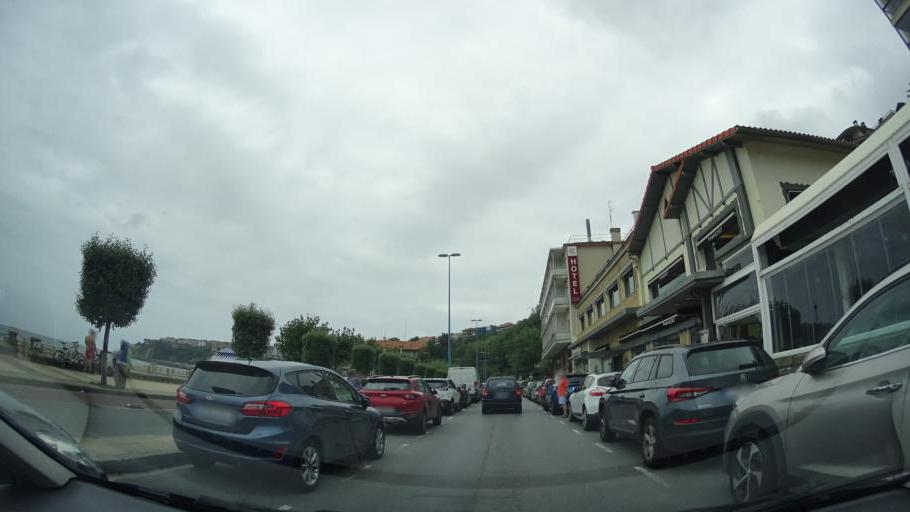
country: ES
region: Basque Country
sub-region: Bizkaia
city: Algorta
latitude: 43.3431
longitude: -3.0119
